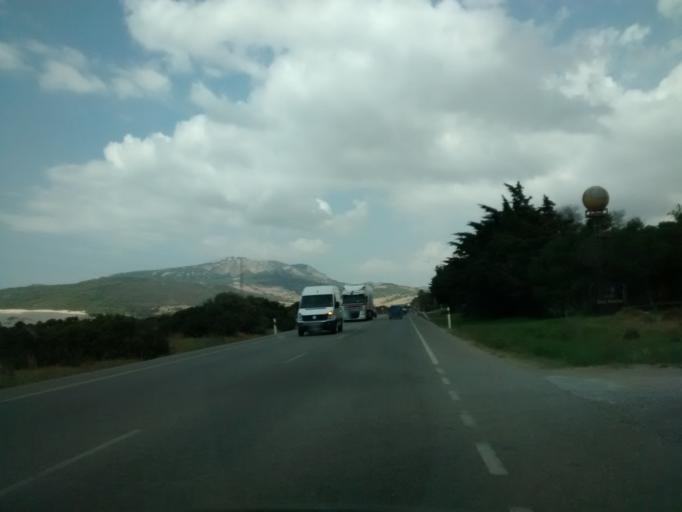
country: ES
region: Andalusia
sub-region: Provincia de Cadiz
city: Tarifa
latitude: 36.0652
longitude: -5.6758
